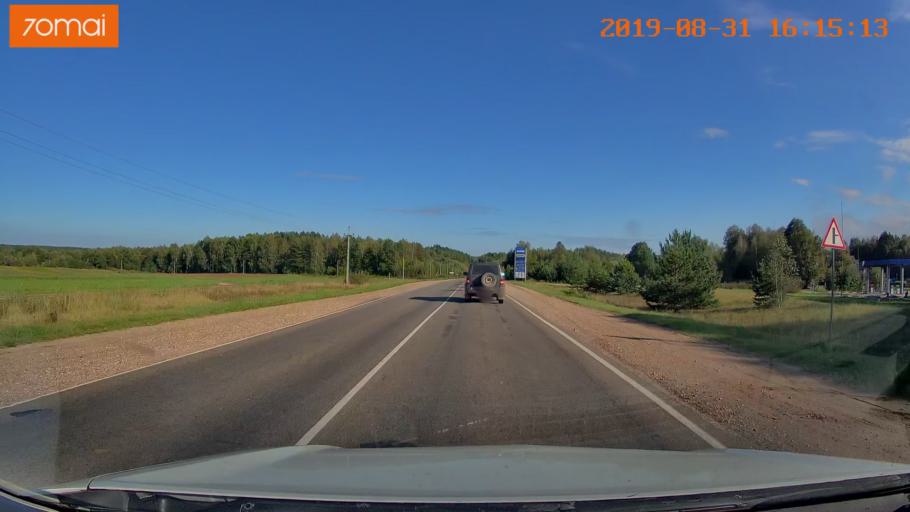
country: RU
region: Kaluga
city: Nikola-Lenivets
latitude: 54.5613
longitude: 35.4837
